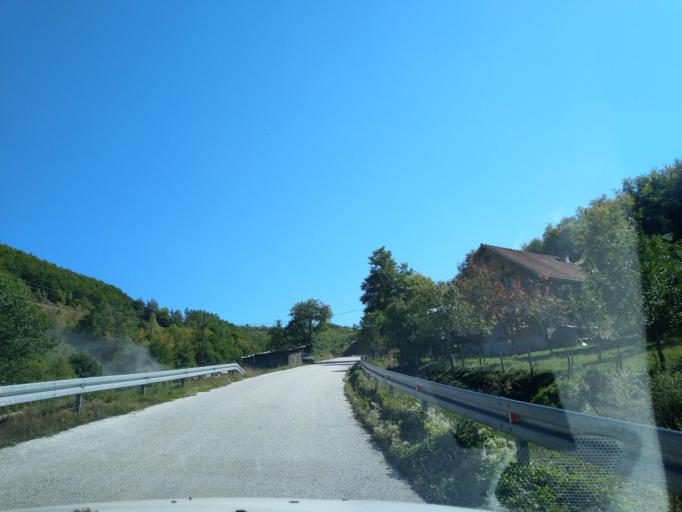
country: RS
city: Sokolovica
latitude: 43.2601
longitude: 20.2992
